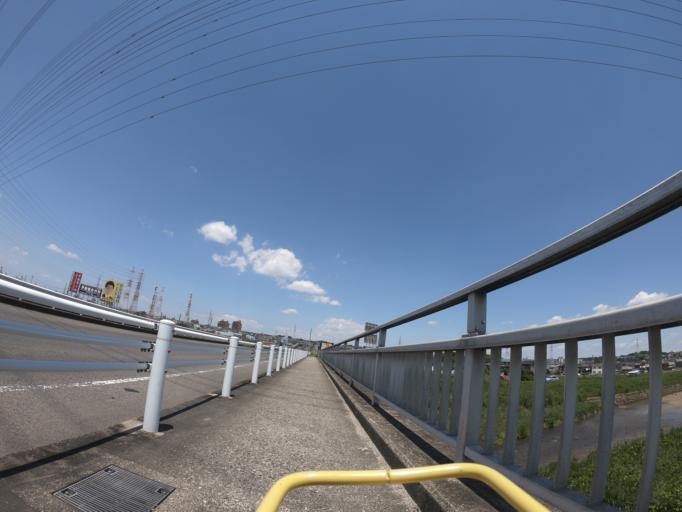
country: JP
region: Aichi
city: Nagoya-shi
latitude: 35.1287
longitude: 137.0154
